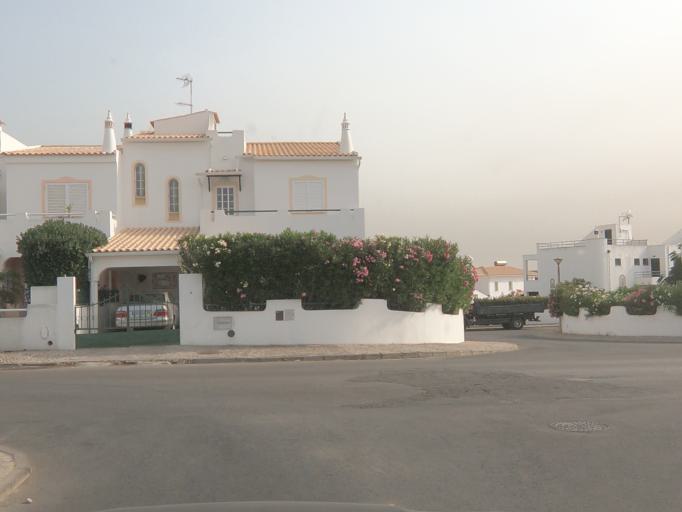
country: PT
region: Faro
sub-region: Albufeira
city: Guia
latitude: 37.0802
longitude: -8.3070
